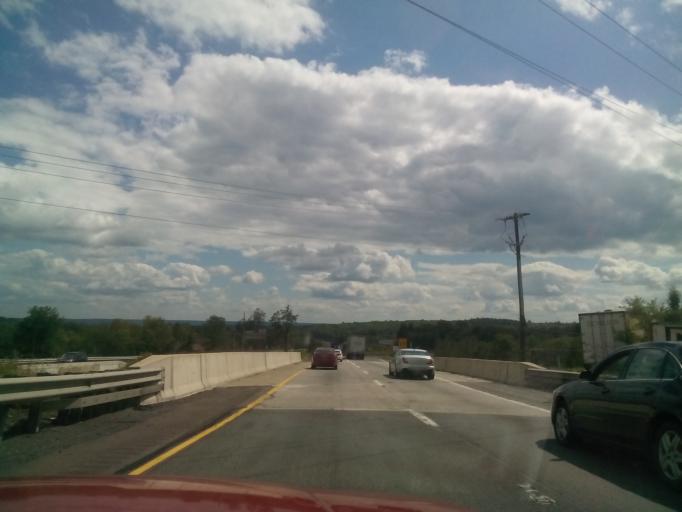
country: US
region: Pennsylvania
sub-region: Monroe County
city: Tannersville
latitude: 41.0410
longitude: -75.3132
